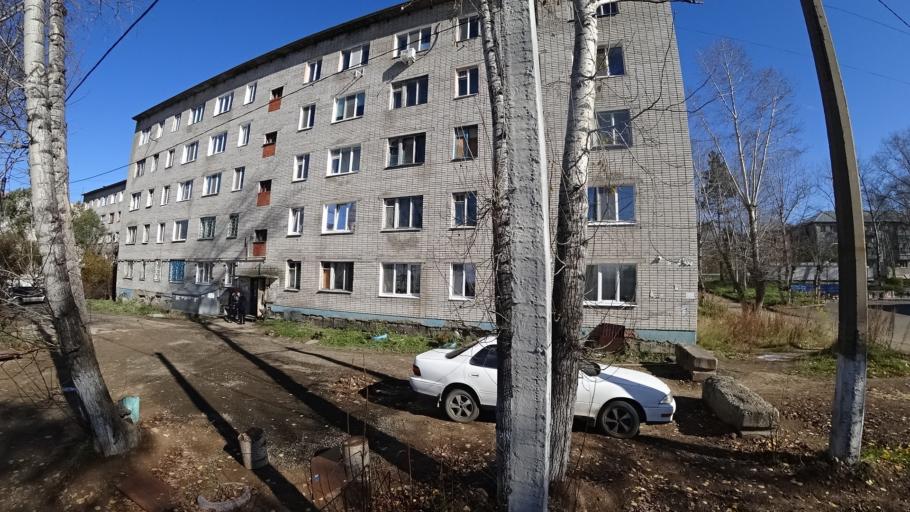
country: RU
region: Khabarovsk Krai
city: Amursk
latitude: 50.2200
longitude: 136.9022
